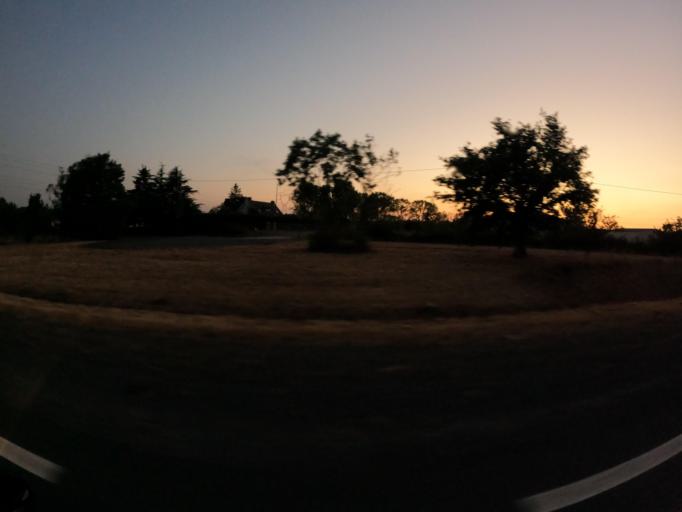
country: FR
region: Pays de la Loire
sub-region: Departement de la Loire-Atlantique
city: Mesanger
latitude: 47.4245
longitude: -1.1872
